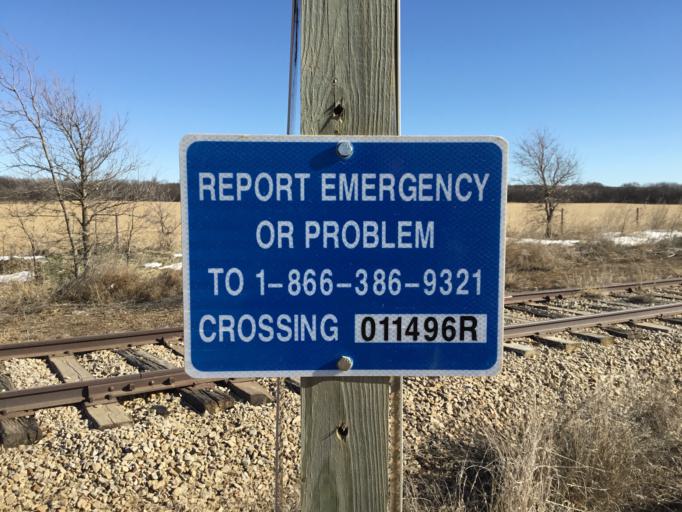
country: US
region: Kansas
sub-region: Lincoln County
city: Lincoln
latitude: 39.1568
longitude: -98.3592
